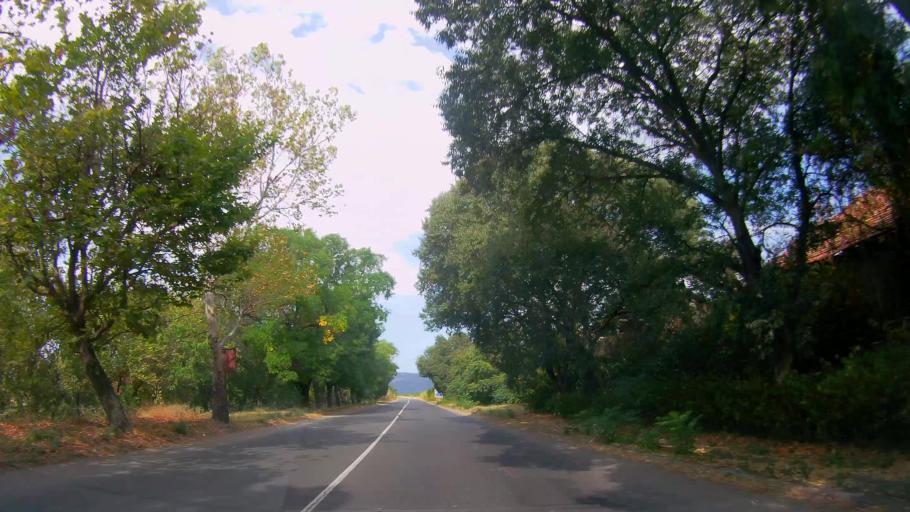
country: BG
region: Burgas
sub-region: Obshtina Aytos
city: Aytos
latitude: 42.7023
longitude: 27.2459
